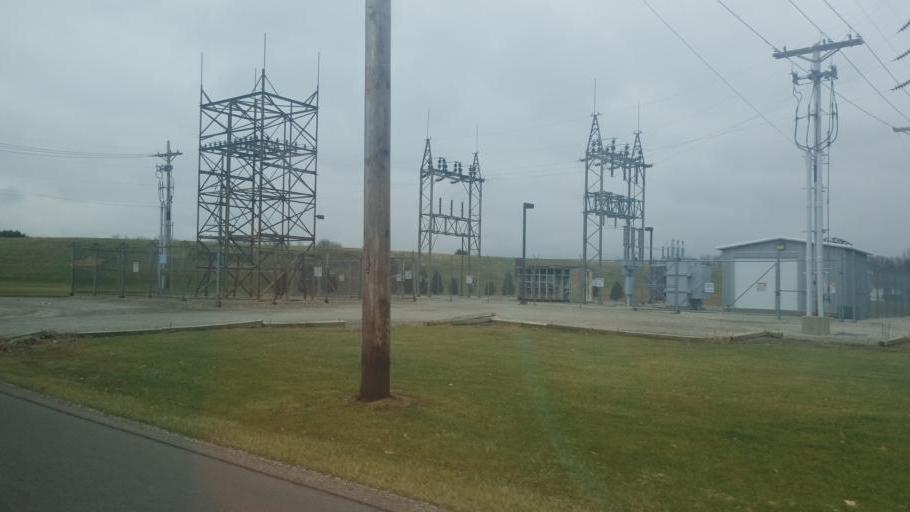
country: US
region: Ohio
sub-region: Crawford County
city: Galion
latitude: 40.7204
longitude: -82.8073
